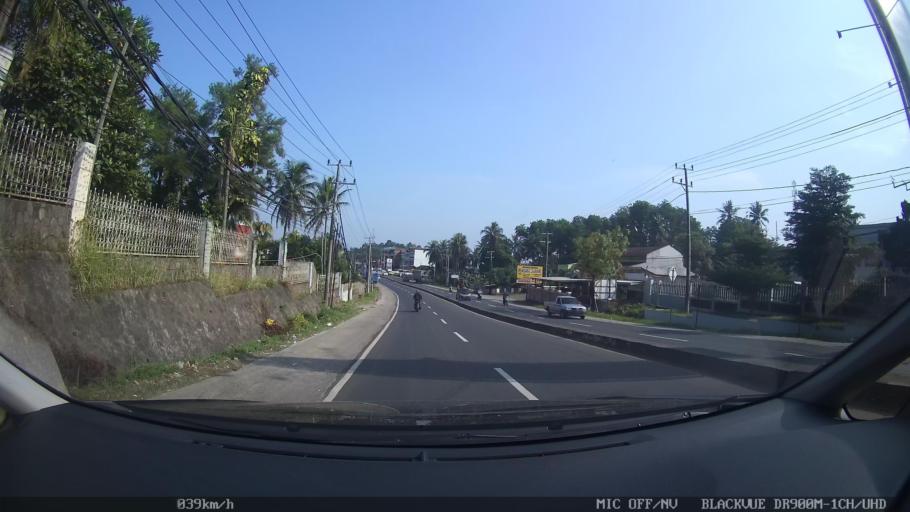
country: ID
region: Lampung
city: Natar
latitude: -5.3492
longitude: 105.2177
